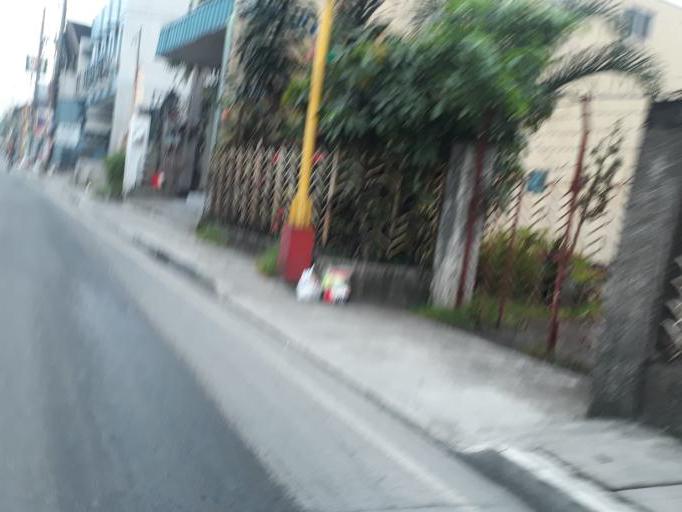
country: PH
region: Calabarzon
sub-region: Province of Rizal
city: Navotas
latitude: 14.6622
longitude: 120.9455
